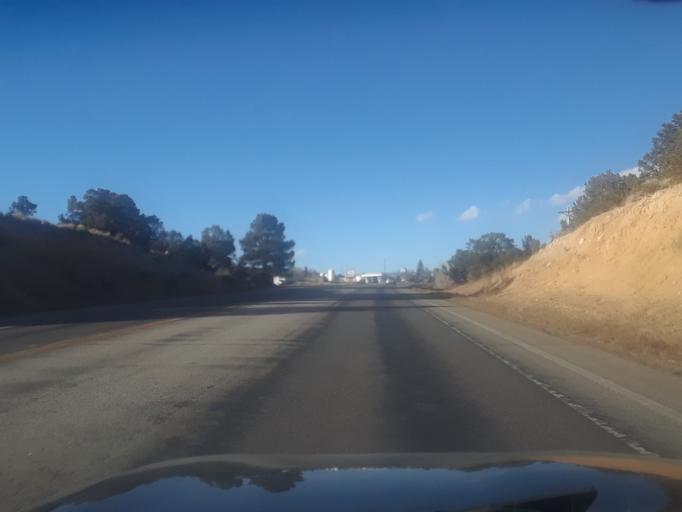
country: US
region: Colorado
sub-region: Chaffee County
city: Salida
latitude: 38.6713
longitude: -106.0908
